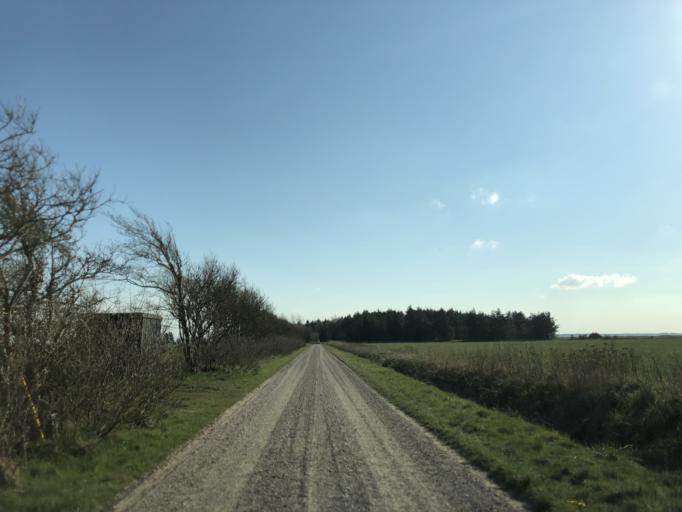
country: DK
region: Central Jutland
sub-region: Holstebro Kommune
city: Ulfborg
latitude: 56.3548
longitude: 8.2484
